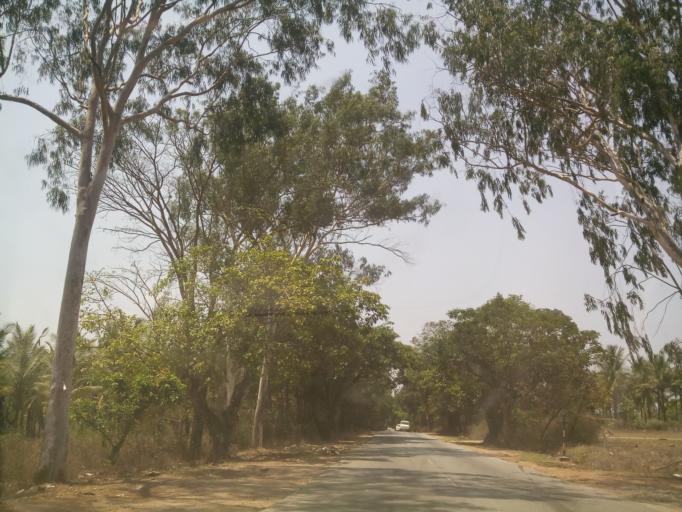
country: IN
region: Karnataka
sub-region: Hassan
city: Alur
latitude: 12.9585
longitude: 75.9830
